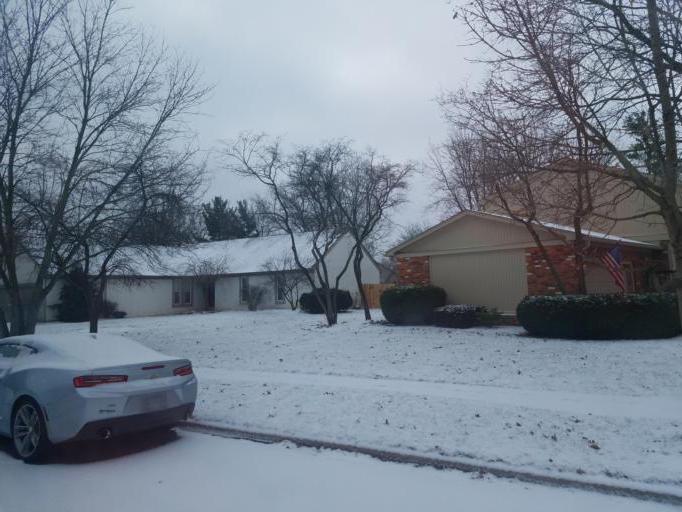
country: US
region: Ohio
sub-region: Delaware County
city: Powell
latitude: 40.1294
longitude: -83.0797
